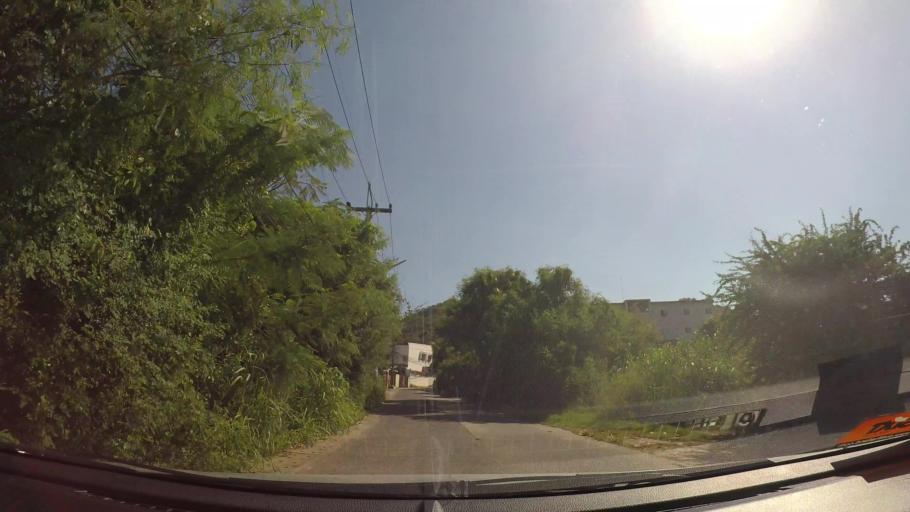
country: TH
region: Chon Buri
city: Si Racha
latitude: 13.1557
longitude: 100.9334
